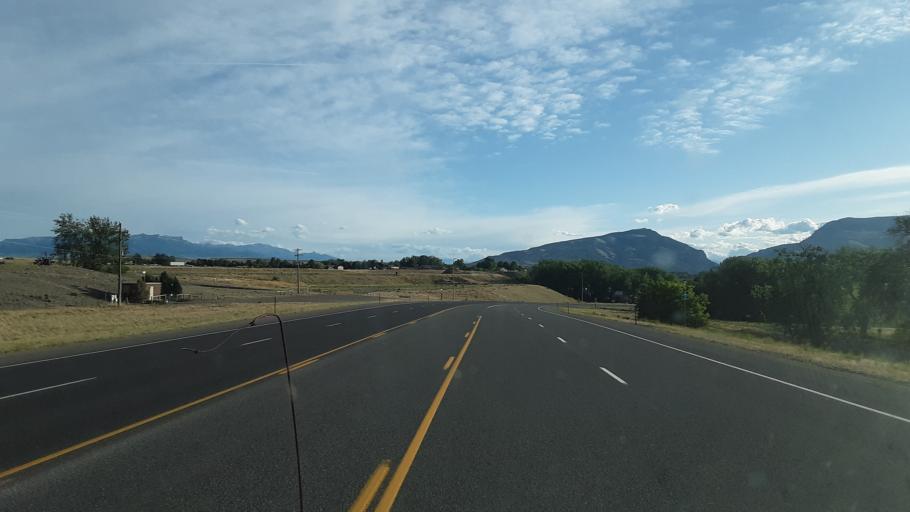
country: US
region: Wyoming
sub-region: Park County
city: Cody
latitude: 44.5349
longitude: -109.0088
